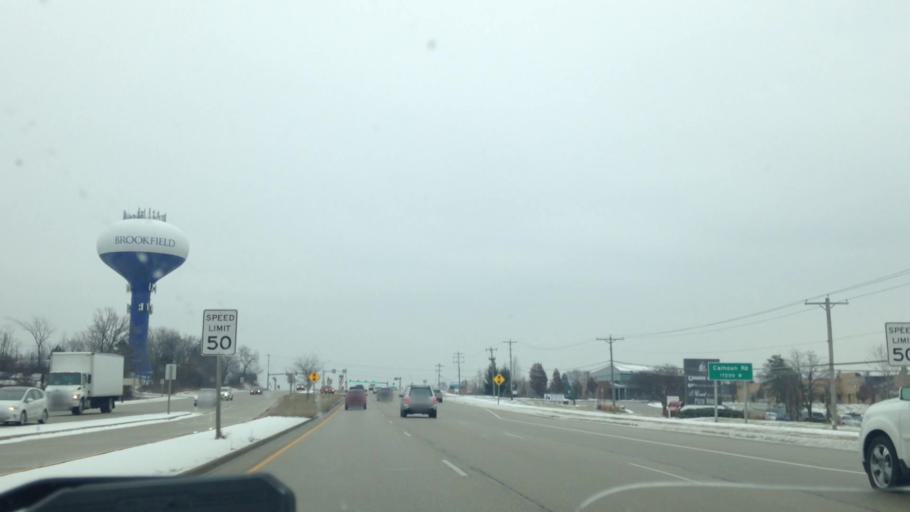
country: US
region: Wisconsin
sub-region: Waukesha County
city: Brookfield
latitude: 43.0902
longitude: -88.1304
